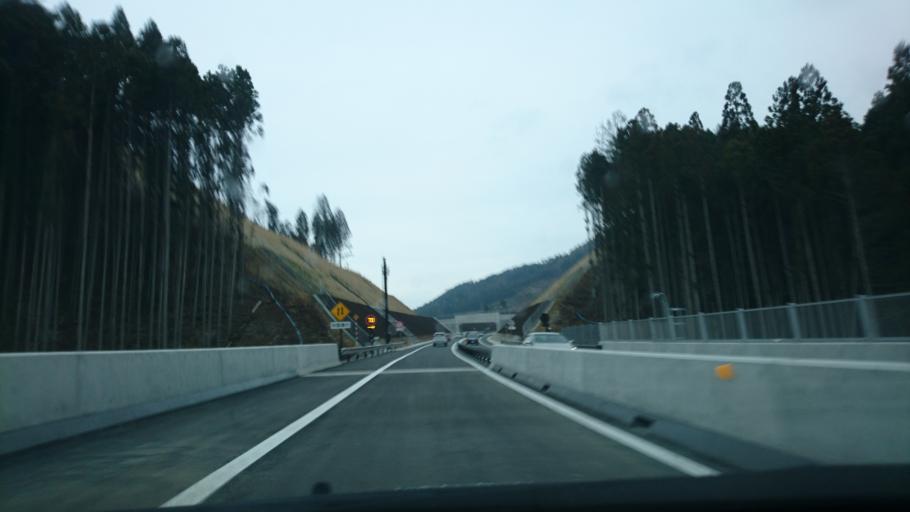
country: JP
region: Iwate
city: Ofunato
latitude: 38.9551
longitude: 141.6274
